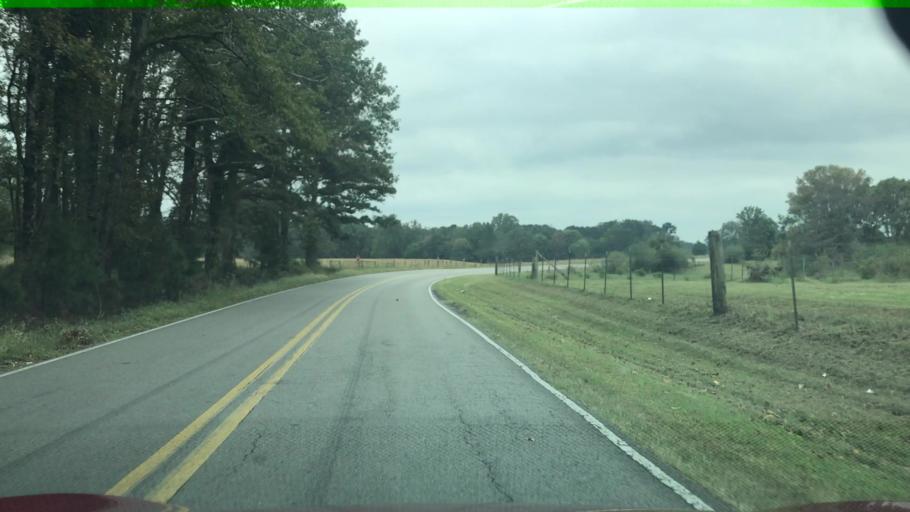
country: US
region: Alabama
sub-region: Cullman County
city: Good Hope
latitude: 34.0980
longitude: -87.0419
